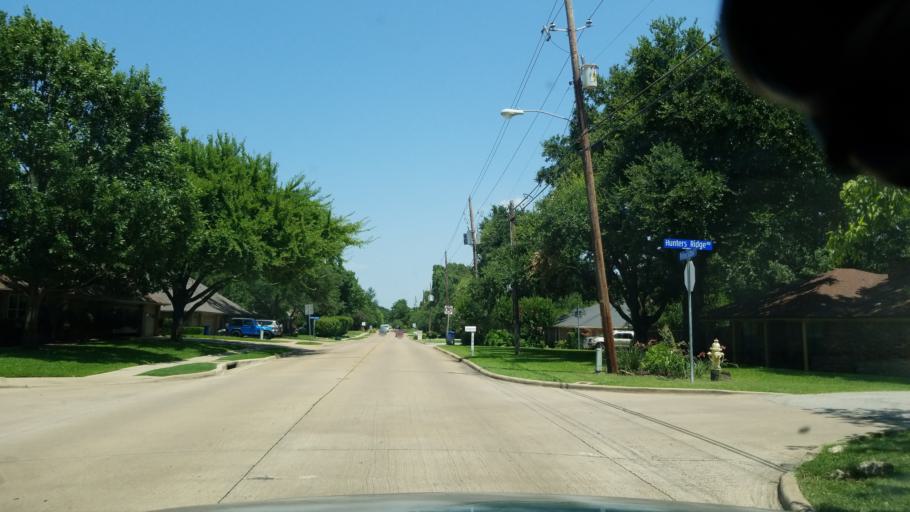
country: US
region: Texas
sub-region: Dallas County
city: Coppell
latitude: 32.9599
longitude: -96.9878
